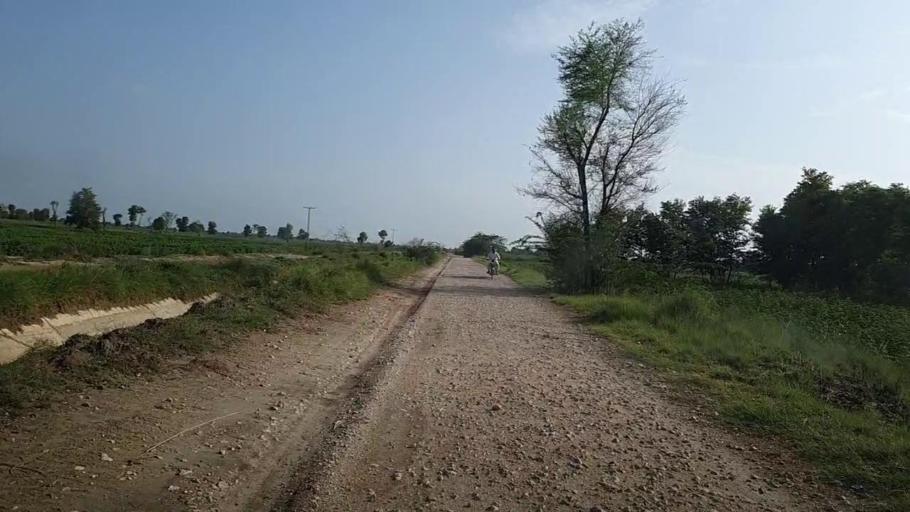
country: PK
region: Sindh
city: Pad Idan
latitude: 26.8317
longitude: 68.2420
